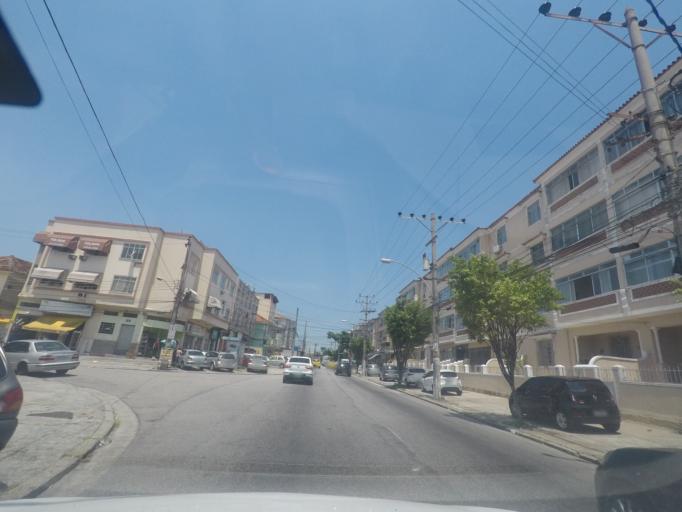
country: BR
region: Rio de Janeiro
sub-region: Duque De Caxias
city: Duque de Caxias
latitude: -22.8397
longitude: -43.2980
